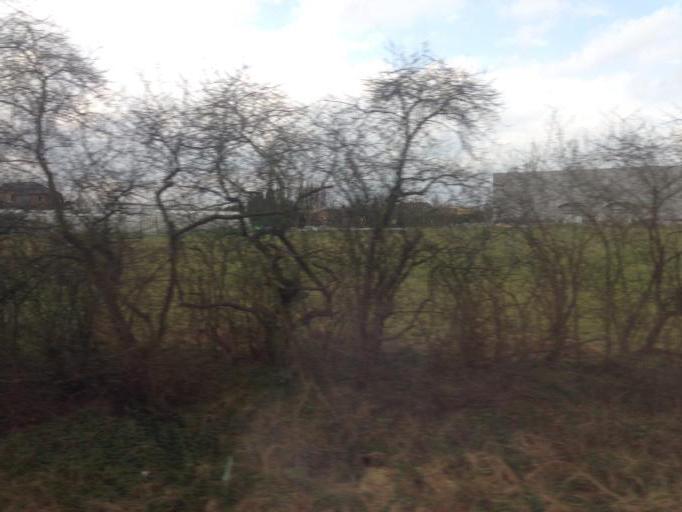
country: DE
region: North Rhine-Westphalia
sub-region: Regierungsbezirk Munster
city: Nottuln
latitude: 51.8687
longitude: 7.3860
